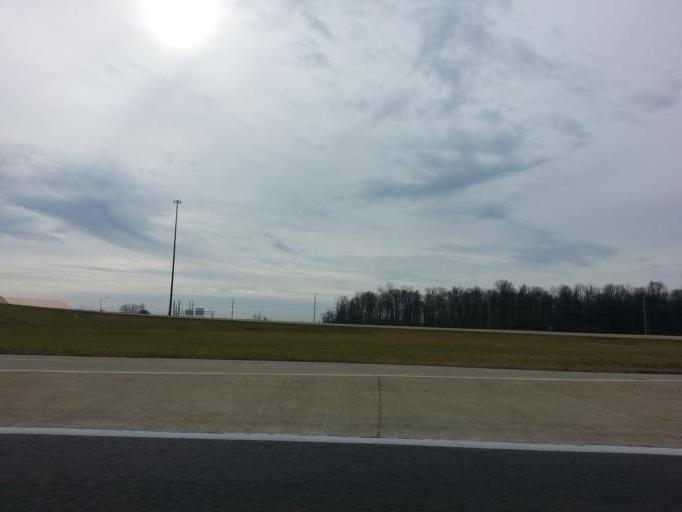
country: US
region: Indiana
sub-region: Decatur County
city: Greensburg
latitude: 39.3627
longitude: -85.5164
